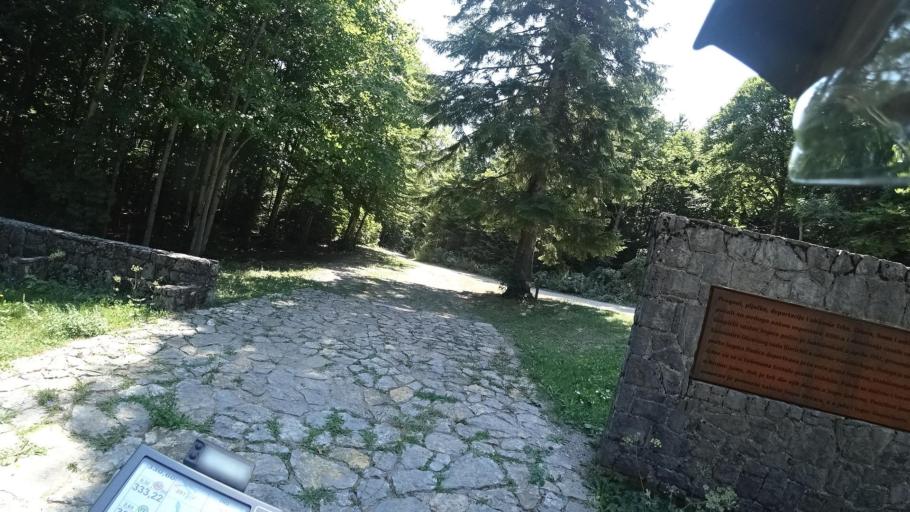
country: HR
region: Licko-Senjska
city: Popovaca
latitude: 44.5449
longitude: 15.2207
